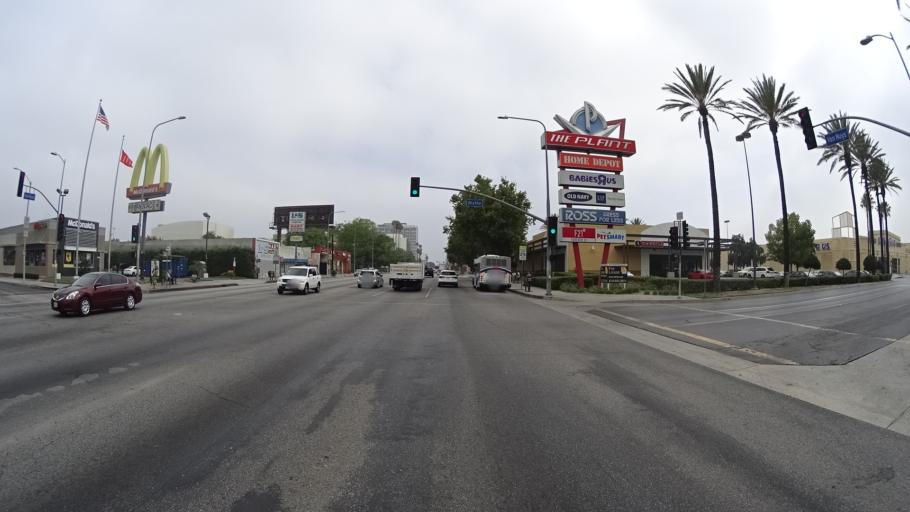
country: US
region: California
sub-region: Los Angeles County
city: Van Nuys
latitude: 34.2150
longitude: -118.4487
